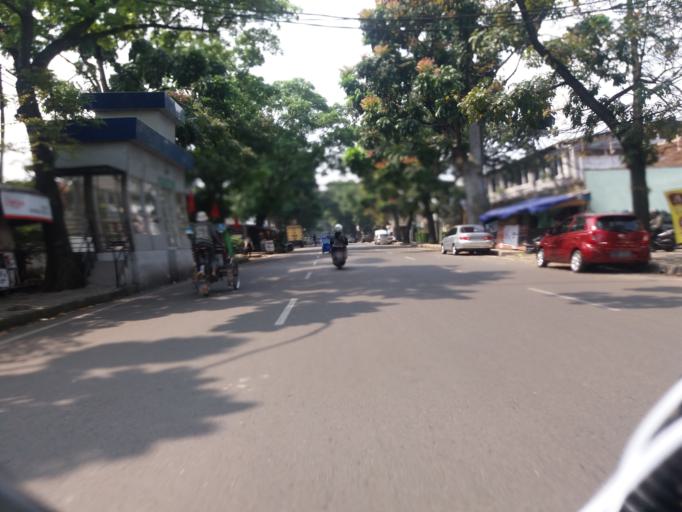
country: ID
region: West Java
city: Bandung
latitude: -6.9138
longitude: 107.5780
